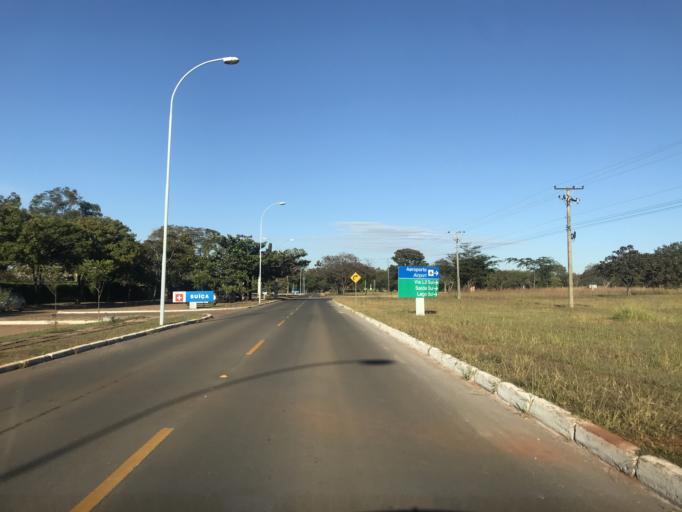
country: BR
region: Federal District
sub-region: Brasilia
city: Brasilia
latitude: -15.8304
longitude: -47.8981
